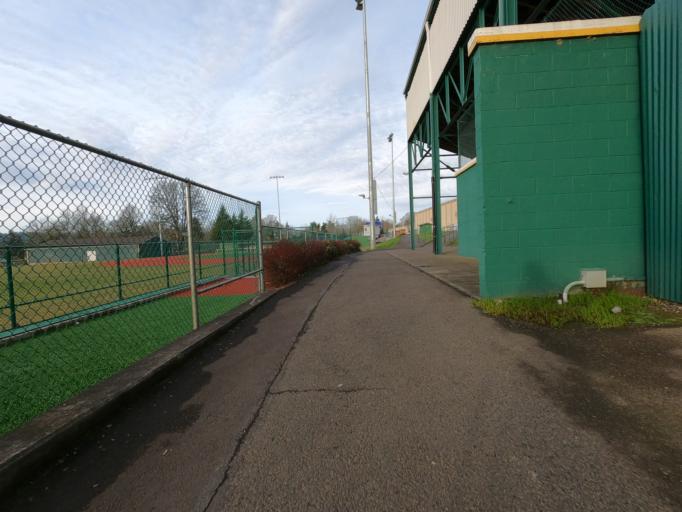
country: US
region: Oregon
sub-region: Clackamas County
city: Jennings Lodge
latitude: 45.3989
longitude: -122.6083
